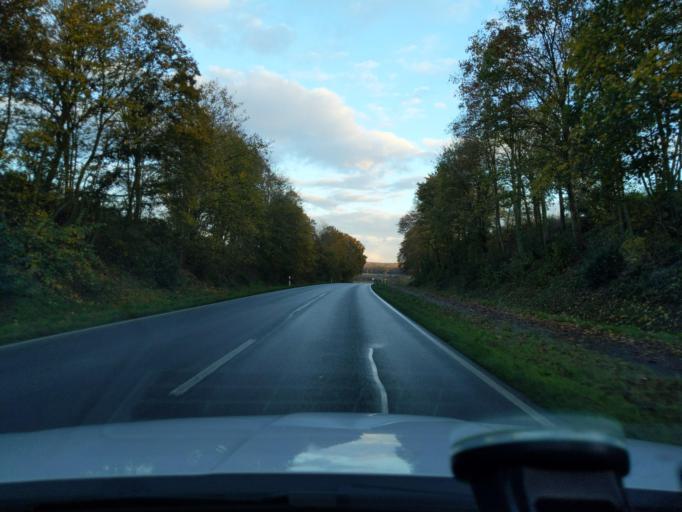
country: DE
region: North Rhine-Westphalia
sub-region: Regierungsbezirk Dusseldorf
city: Uedem
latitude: 51.6720
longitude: 6.2921
